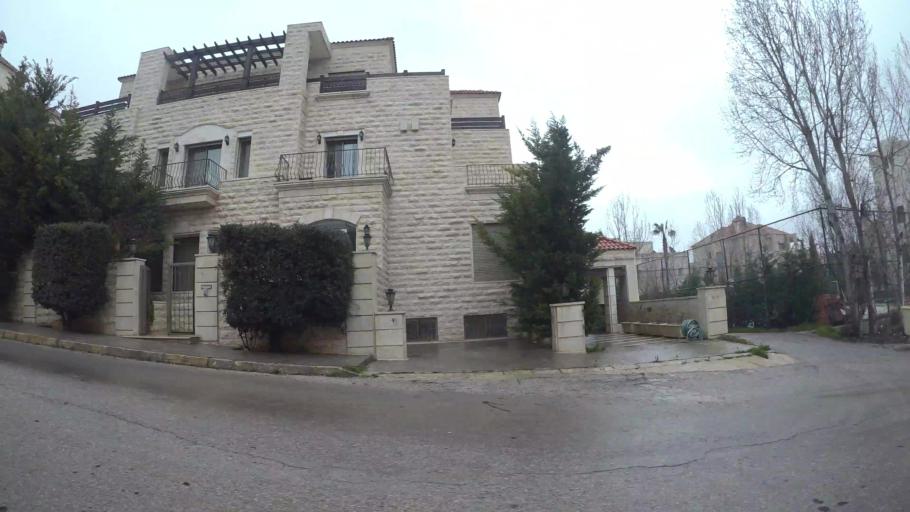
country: JO
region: Amman
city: Al Jubayhah
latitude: 32.0117
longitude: 35.8253
